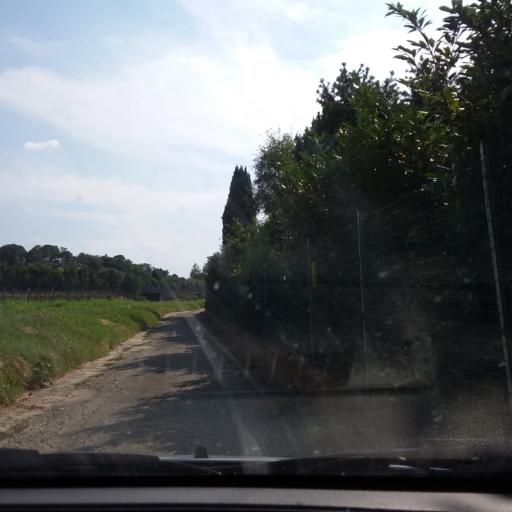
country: IT
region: Piedmont
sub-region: Provincia di Torino
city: Rivoli
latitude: 45.0864
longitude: 7.5357
